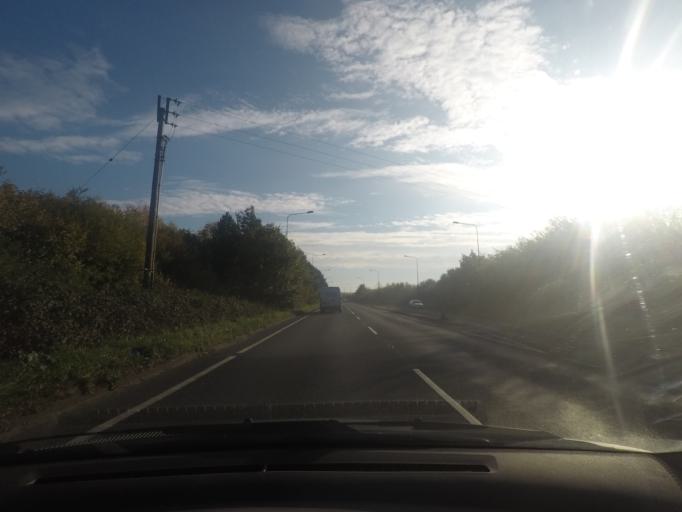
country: GB
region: England
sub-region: East Riding of Yorkshire
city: Market Weighton
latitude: 53.8575
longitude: -0.6692
